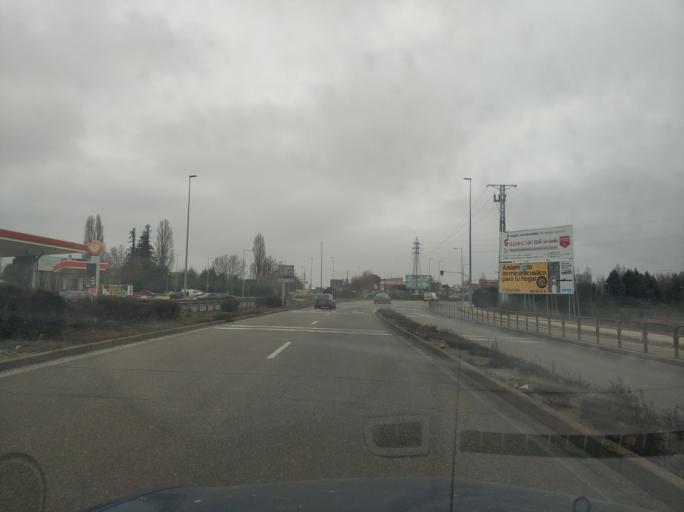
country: ES
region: Castille and Leon
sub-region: Provincia de Valladolid
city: Cisterniga
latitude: 41.6313
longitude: -4.7033
